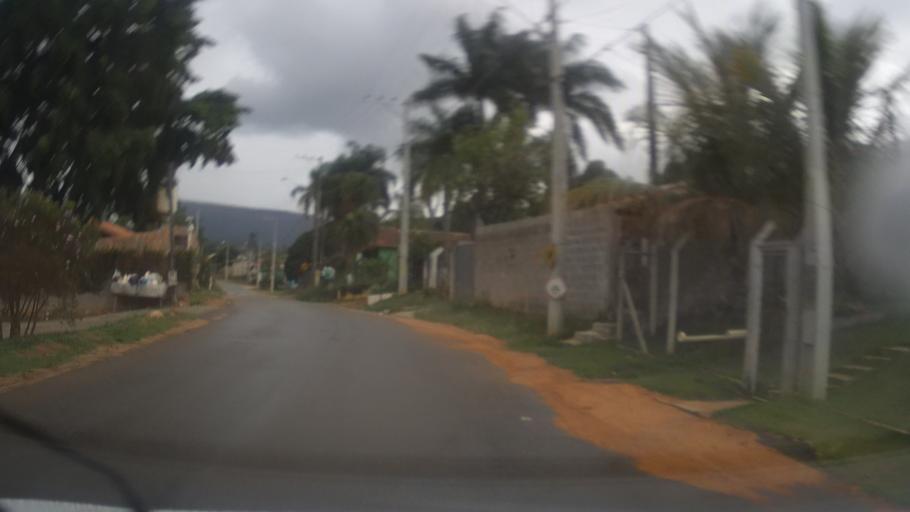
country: BR
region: Sao Paulo
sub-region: Itupeva
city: Itupeva
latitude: -23.1865
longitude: -47.0156
